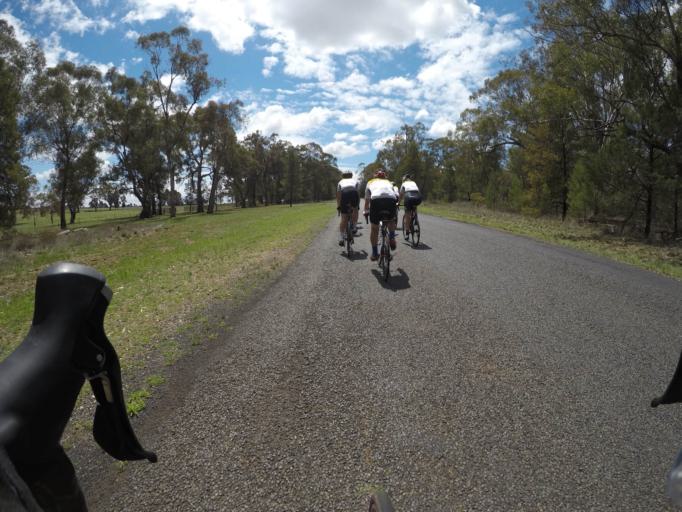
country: AU
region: New South Wales
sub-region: Dubbo Municipality
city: Dubbo
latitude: -32.3816
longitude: 148.5756
